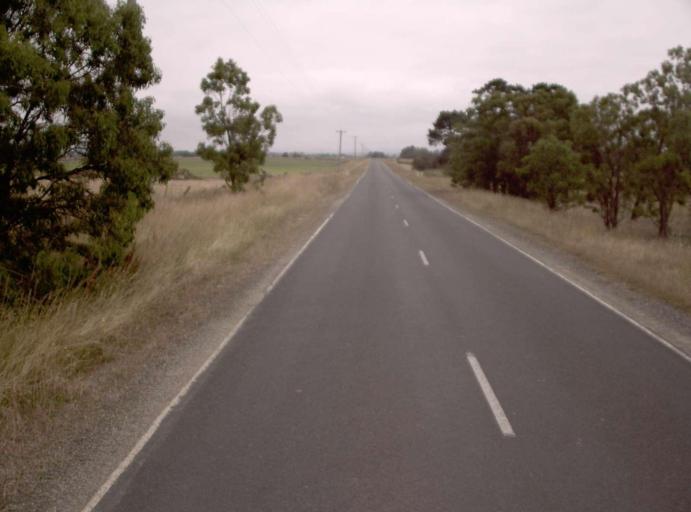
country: AU
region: Victoria
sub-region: Wellington
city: Heyfield
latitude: -38.0360
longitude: 146.7665
